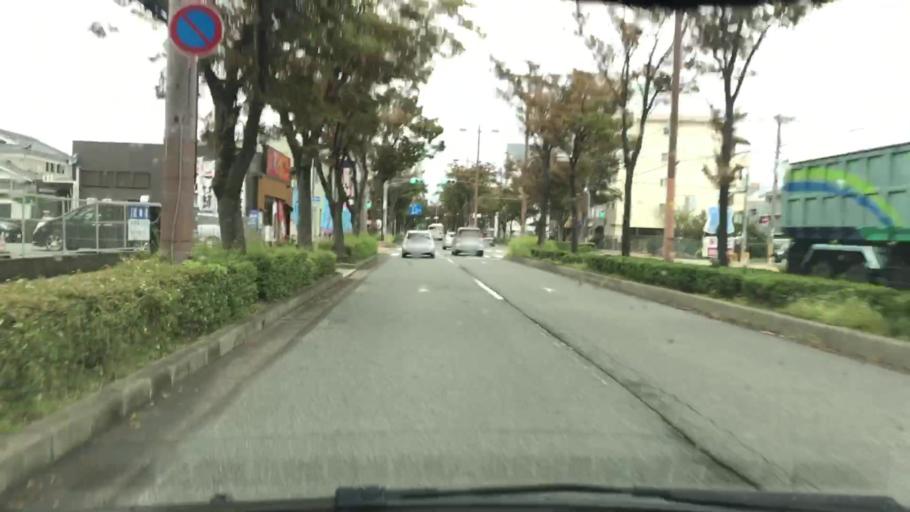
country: JP
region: Hyogo
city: Amagasaki
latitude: 34.7445
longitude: 135.3960
